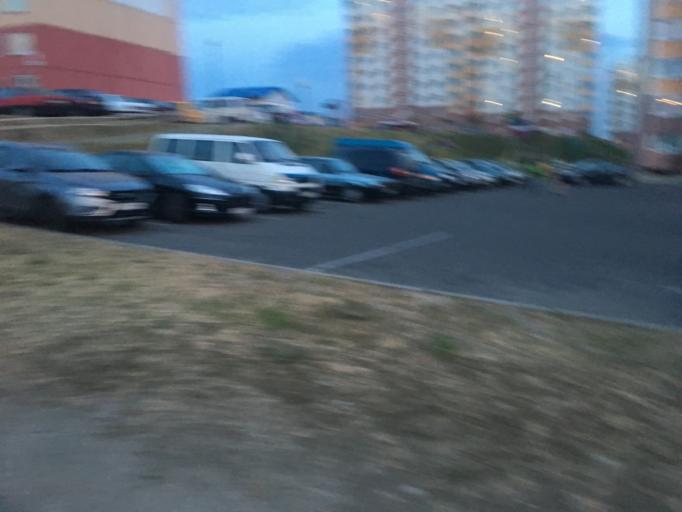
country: BY
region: Grodnenskaya
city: Hrodna
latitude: 53.7133
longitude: 23.8678
